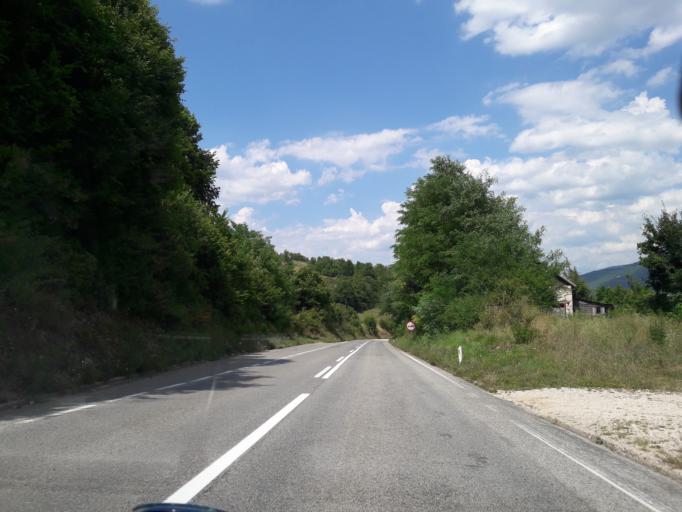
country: BA
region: Republika Srpska
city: Mrkonjic Grad
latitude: 44.5040
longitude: 17.1504
